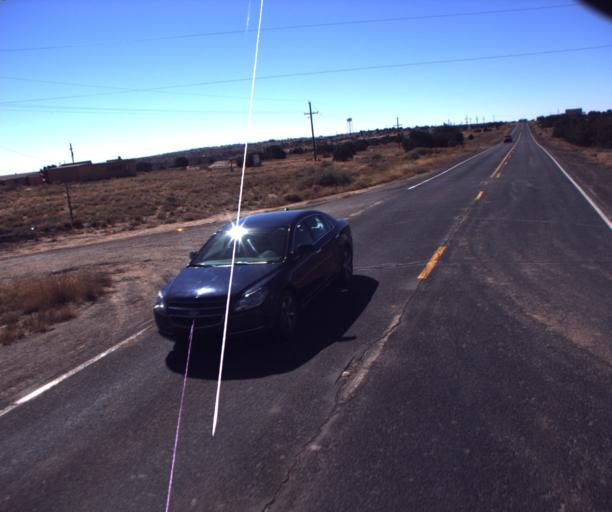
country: US
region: Arizona
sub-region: Navajo County
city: First Mesa
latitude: 35.8337
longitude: -110.5291
